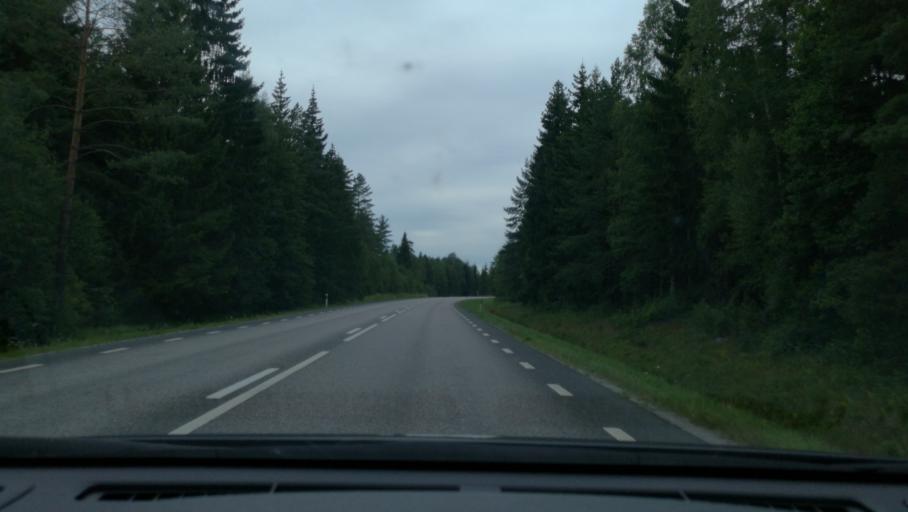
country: SE
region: Soedermanland
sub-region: Katrineholms Kommun
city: Katrineholm
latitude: 59.0760
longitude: 16.2133
